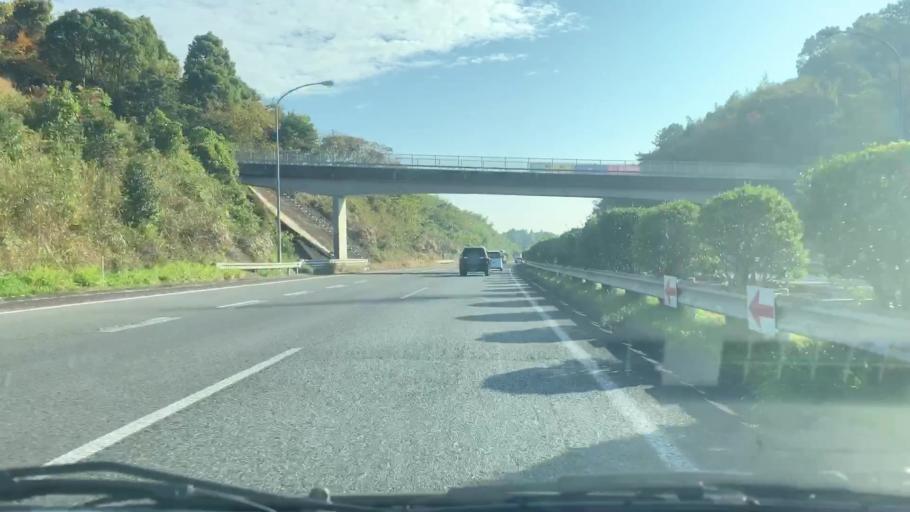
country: JP
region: Saga Prefecture
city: Saga-shi
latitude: 33.3113
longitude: 130.2117
